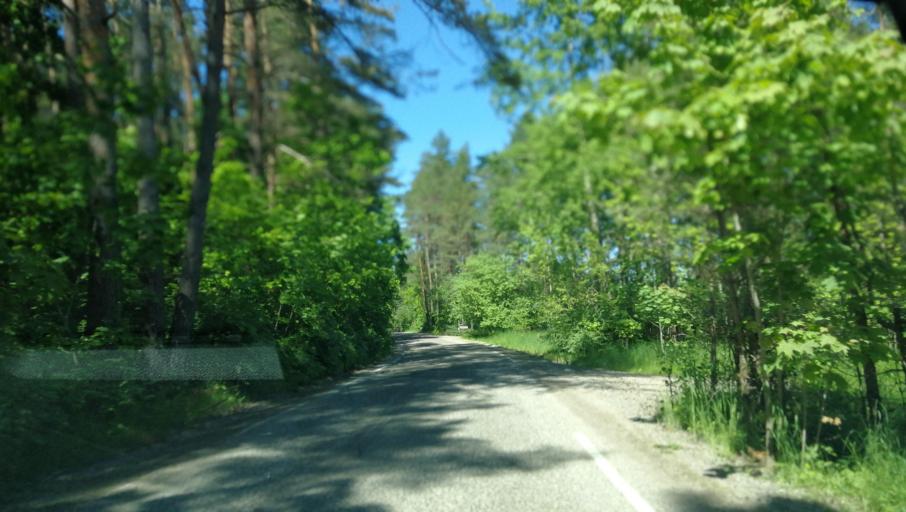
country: LV
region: Kekava
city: Kekava
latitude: 56.8588
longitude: 24.2500
